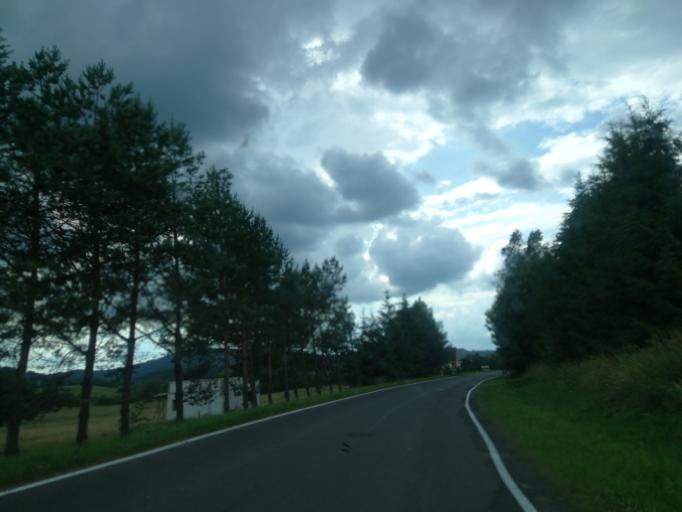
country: PL
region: Subcarpathian Voivodeship
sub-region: Powiat leski
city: Uherce Mineralne
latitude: 49.4527
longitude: 22.4243
